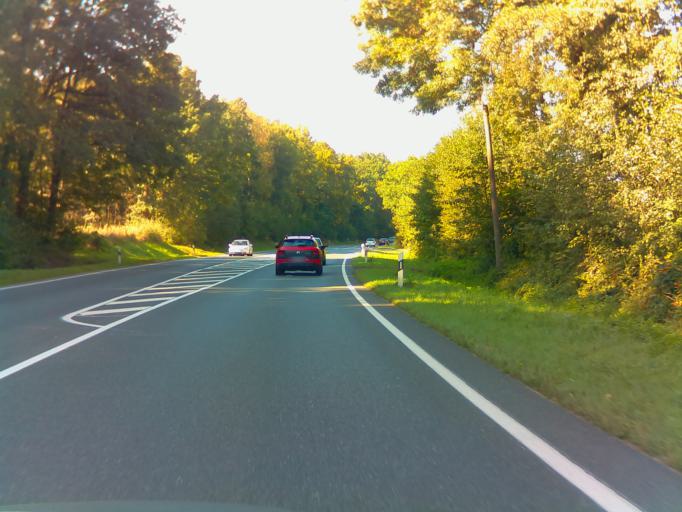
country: DE
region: Bavaria
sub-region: Upper Franconia
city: Michelau
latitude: 50.1500
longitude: 11.1286
